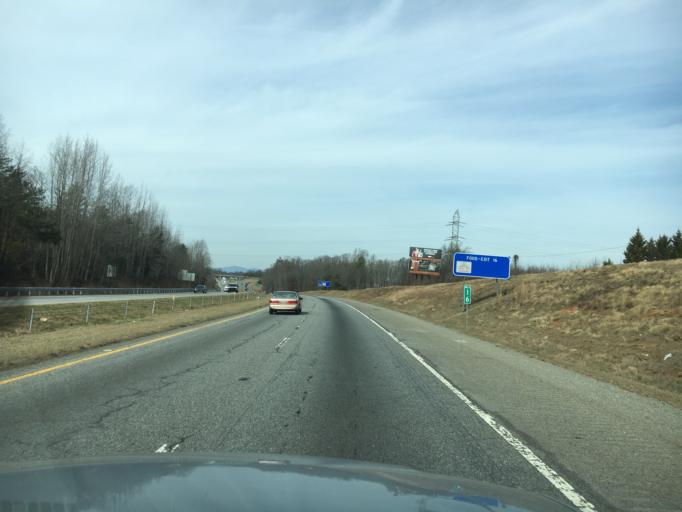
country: US
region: South Carolina
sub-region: Spartanburg County
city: Southern Shops
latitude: 35.0011
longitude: -82.0212
